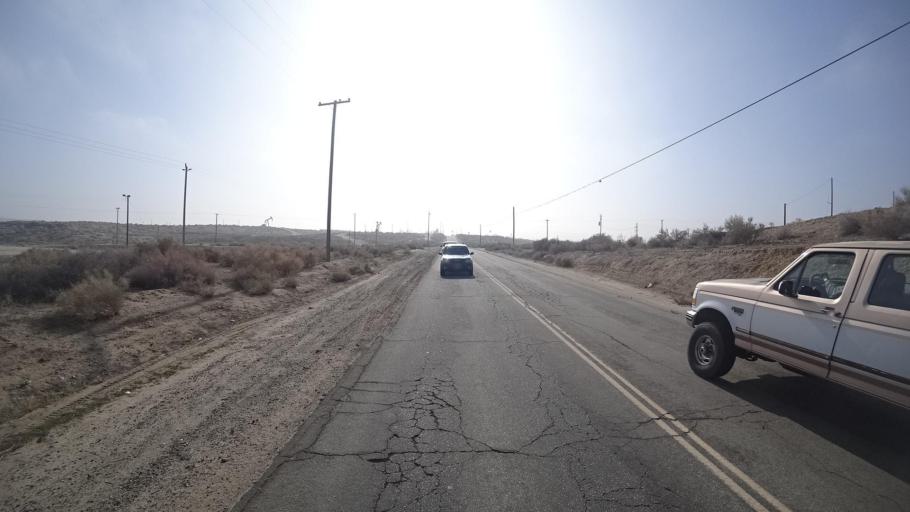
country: US
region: California
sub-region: Kern County
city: Ford City
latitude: 35.1755
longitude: -119.4654
